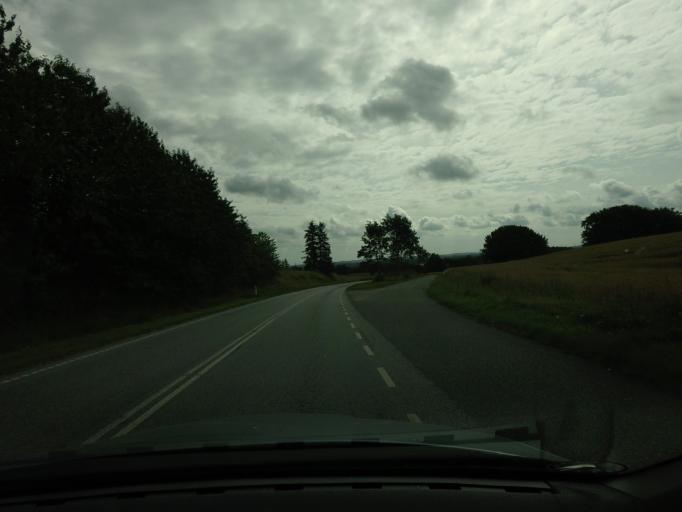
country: DK
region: North Denmark
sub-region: Hjorring Kommune
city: Tars
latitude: 57.2856
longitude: 10.2180
